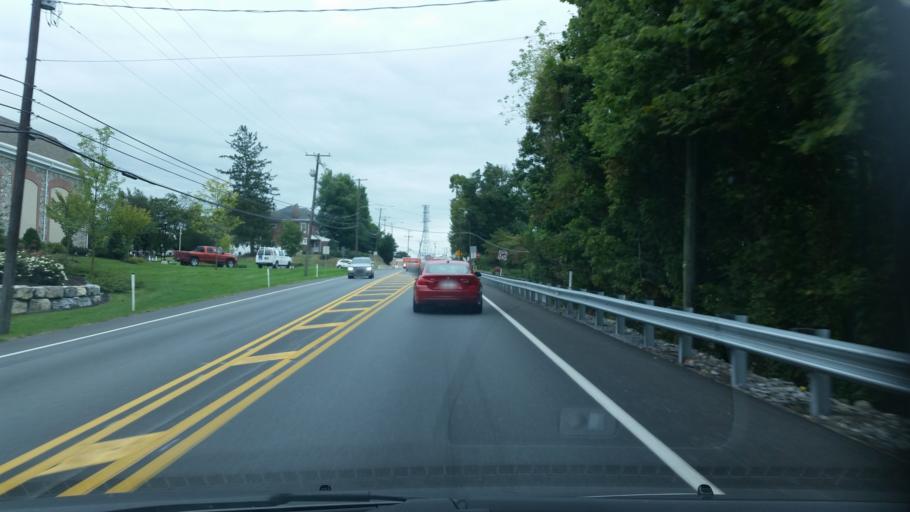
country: US
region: Pennsylvania
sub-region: Lancaster County
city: Willow Street
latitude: 39.9953
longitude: -76.2883
